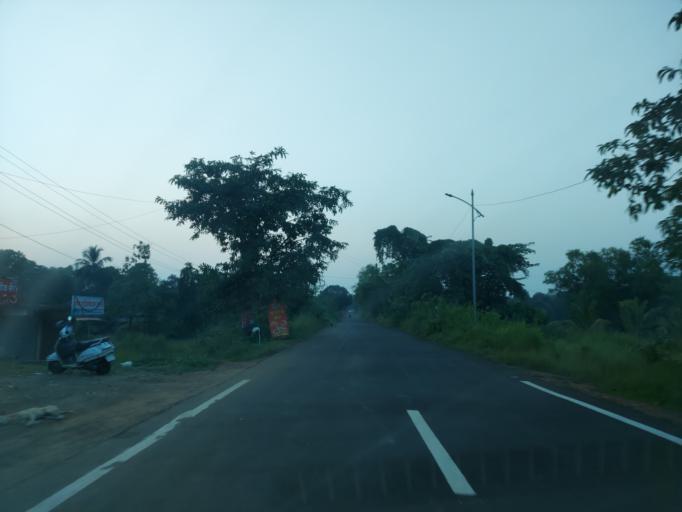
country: IN
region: Maharashtra
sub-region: Sindhudurg
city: Kudal
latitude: 16.1036
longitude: 73.7083
